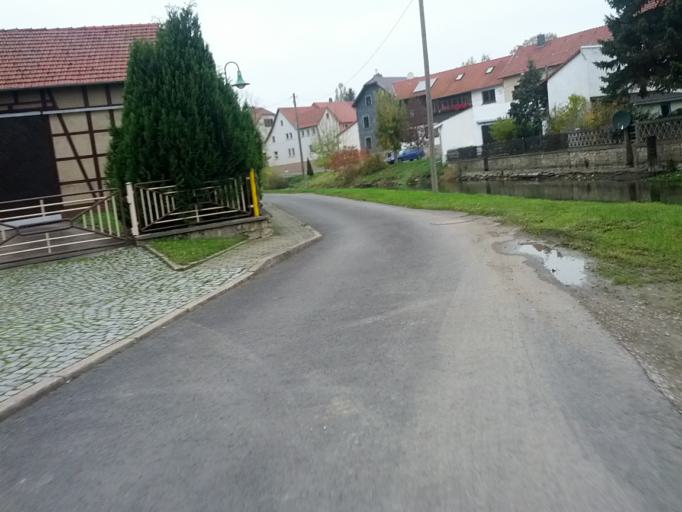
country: DE
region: Thuringia
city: Seebach
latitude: 50.9804
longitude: 10.4279
